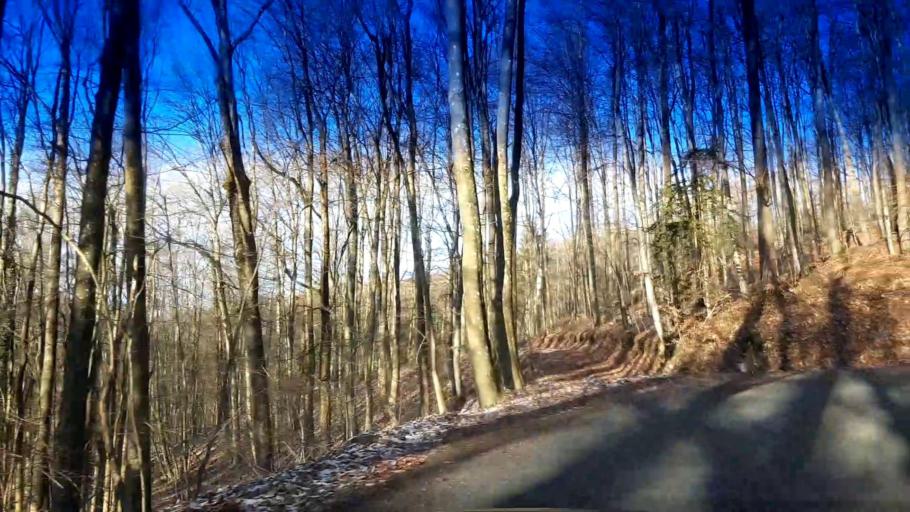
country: DE
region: Bavaria
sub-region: Upper Franconia
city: Buttenheim
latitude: 49.8360
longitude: 11.0800
